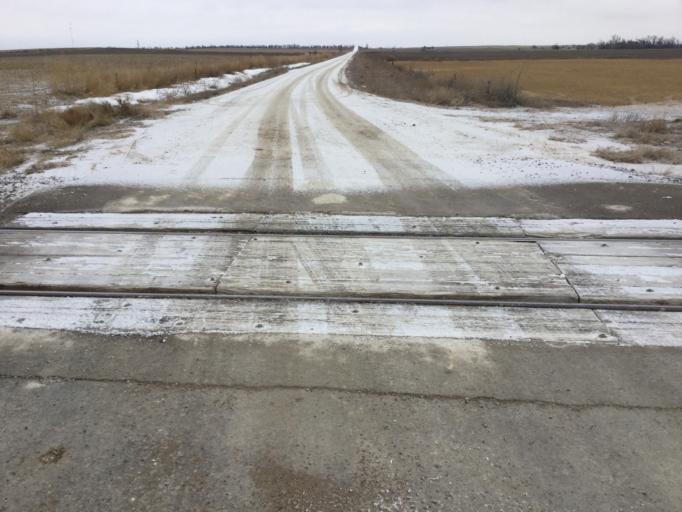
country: US
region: Kansas
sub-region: Ellis County
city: Ellis
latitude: 38.9377
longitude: -99.5947
